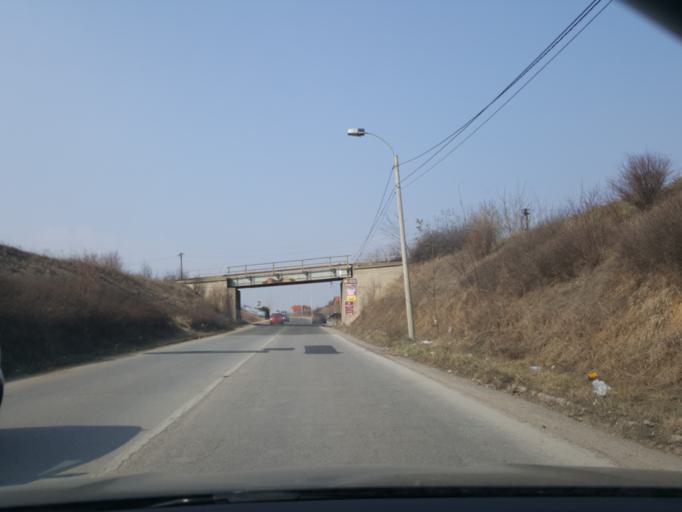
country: RS
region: Central Serbia
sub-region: Nisavski Okrug
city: Nis
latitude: 43.3412
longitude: 21.8850
